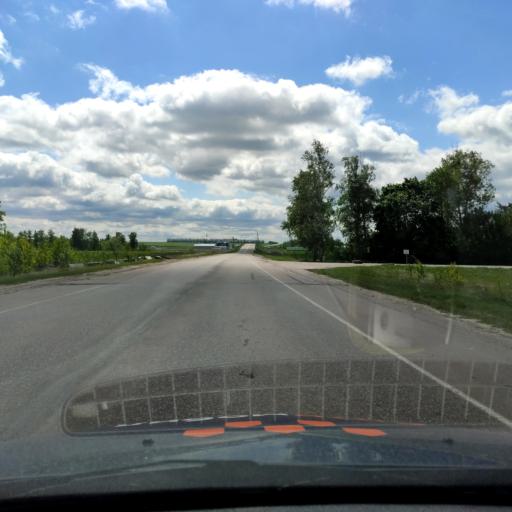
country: RU
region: Voronezj
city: Novaya Usman'
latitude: 51.6082
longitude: 39.3375
